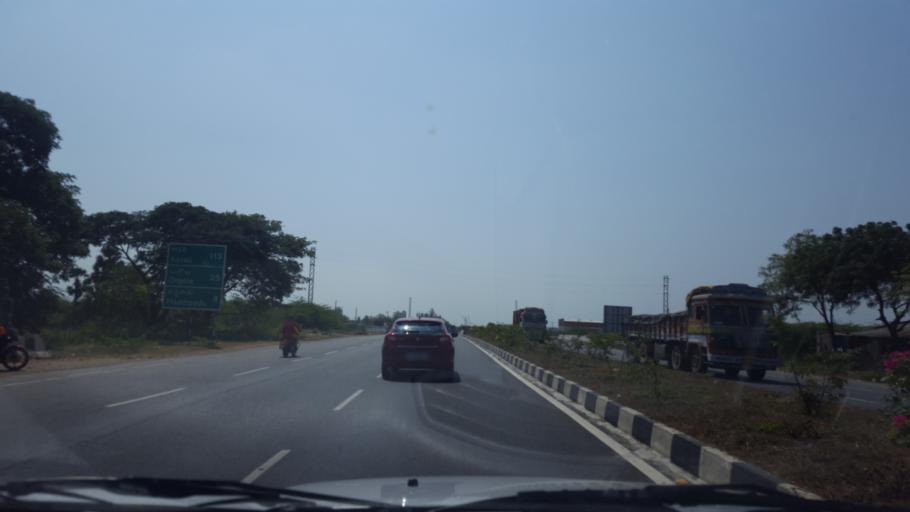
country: IN
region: Andhra Pradesh
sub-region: Prakasam
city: Addanki
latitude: 15.6927
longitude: 80.0185
